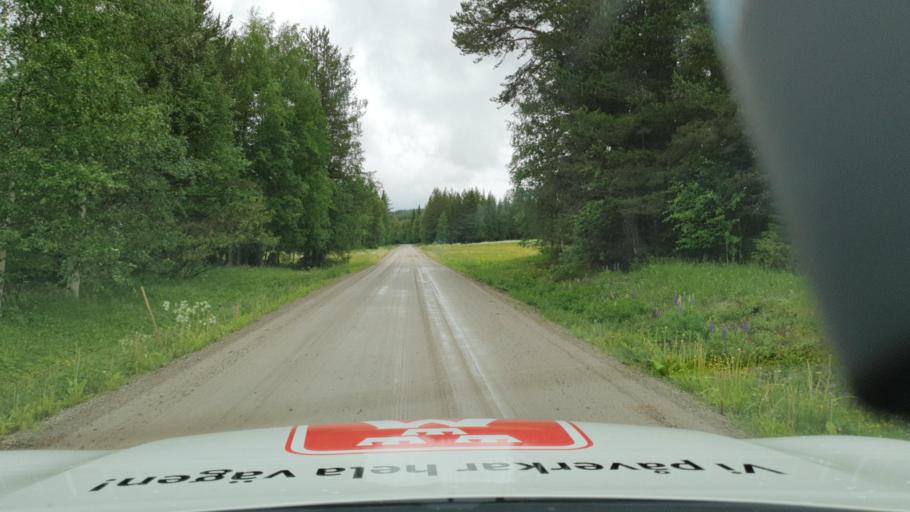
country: SE
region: Vaesterbotten
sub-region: Dorotea Kommun
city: Dorotea
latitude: 64.0252
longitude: 16.7898
